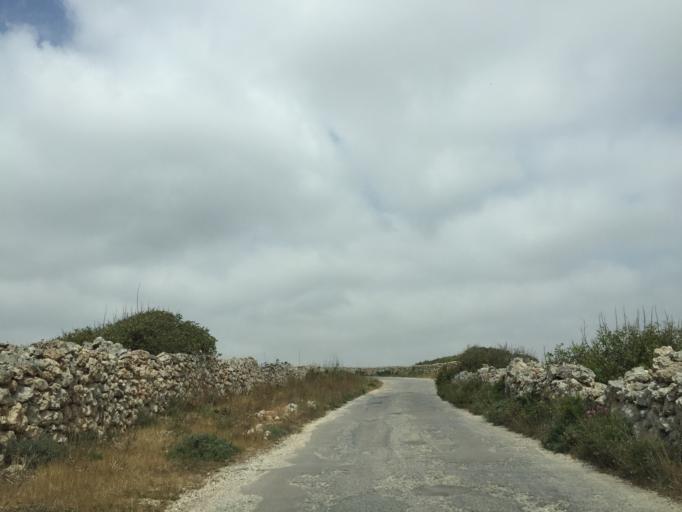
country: MT
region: L-Imgarr
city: Imgarr
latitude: 35.8994
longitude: 14.3705
